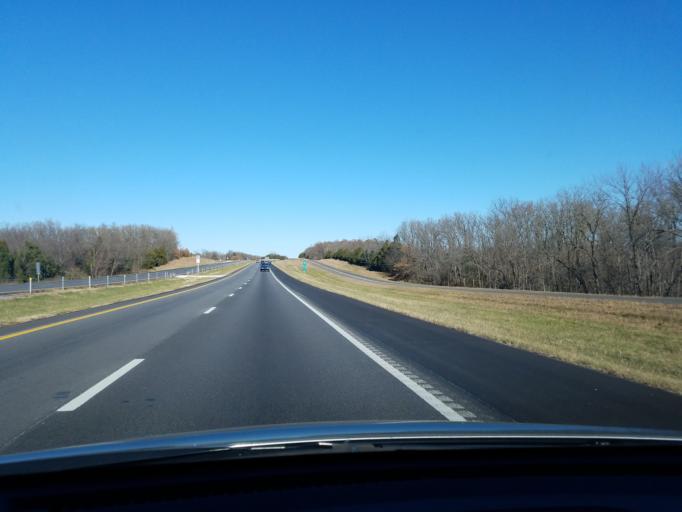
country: US
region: Missouri
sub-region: Webster County
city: Marshfield
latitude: 37.3949
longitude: -92.8983
